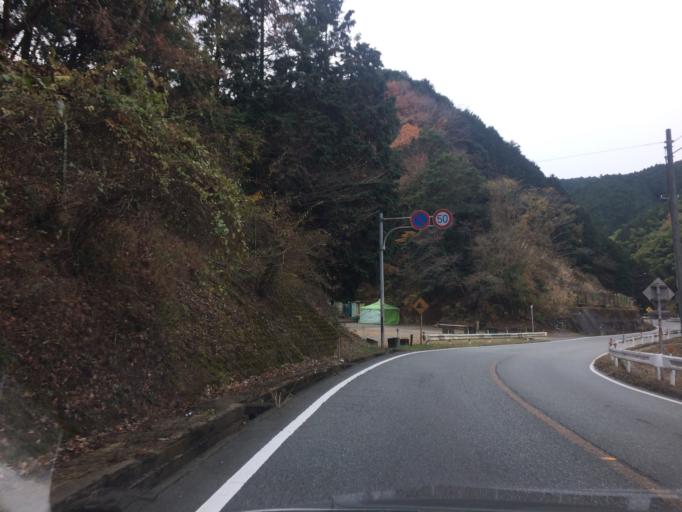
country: JP
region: Shizuoka
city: Fujinomiya
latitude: 35.1872
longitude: 138.5283
